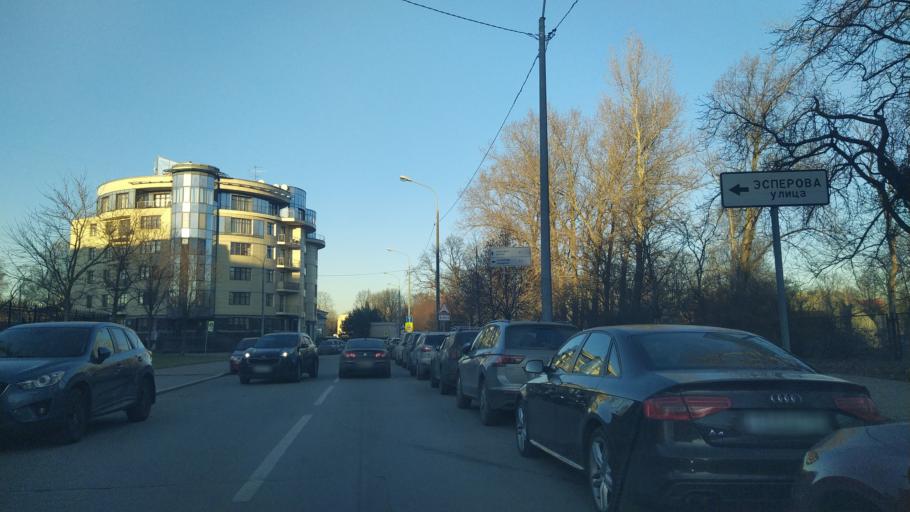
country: RU
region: St.-Petersburg
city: Novaya Derevnya
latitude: 59.9728
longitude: 30.2761
